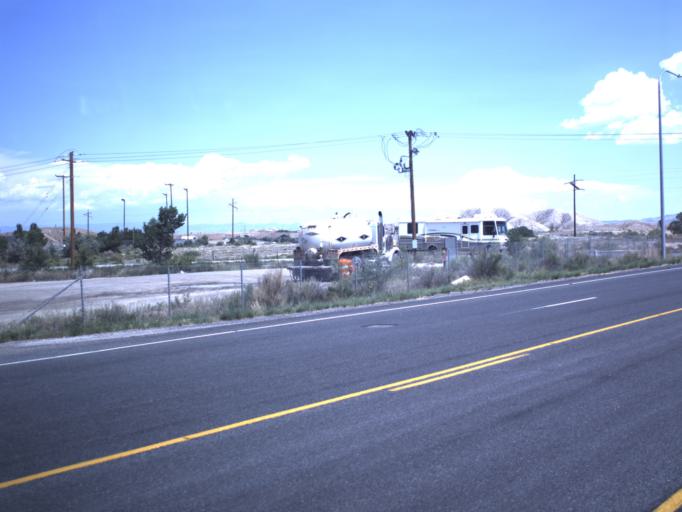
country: US
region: Utah
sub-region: Emery County
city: Huntington
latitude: 39.3368
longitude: -110.9703
